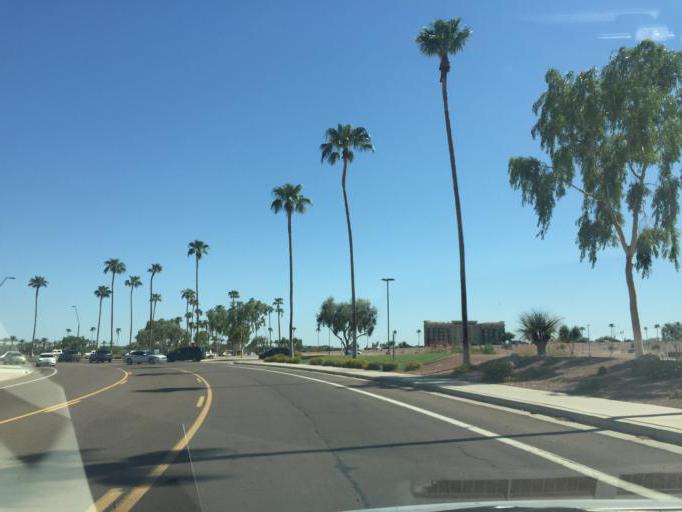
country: US
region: Arizona
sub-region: Maricopa County
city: Guadalupe
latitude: 33.3380
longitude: -111.9694
